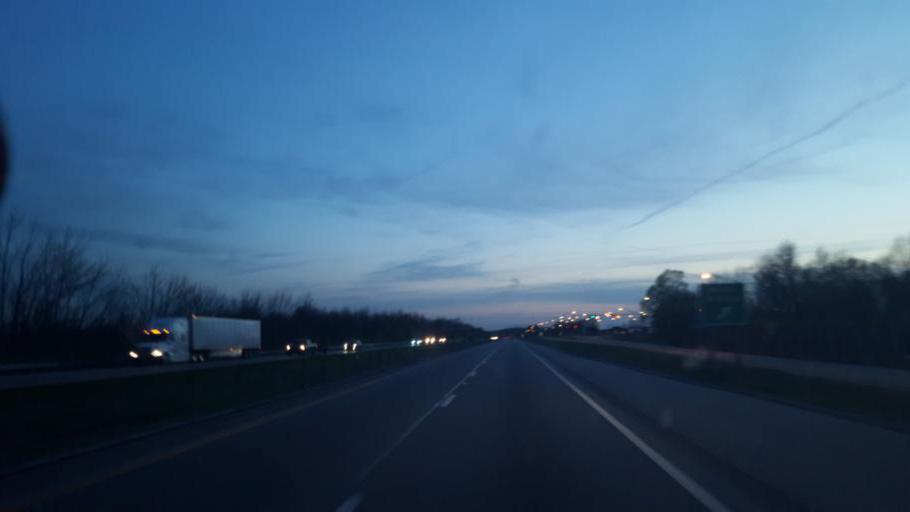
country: US
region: Kentucky
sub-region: Boone County
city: Walton
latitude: 38.8671
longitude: -84.6430
